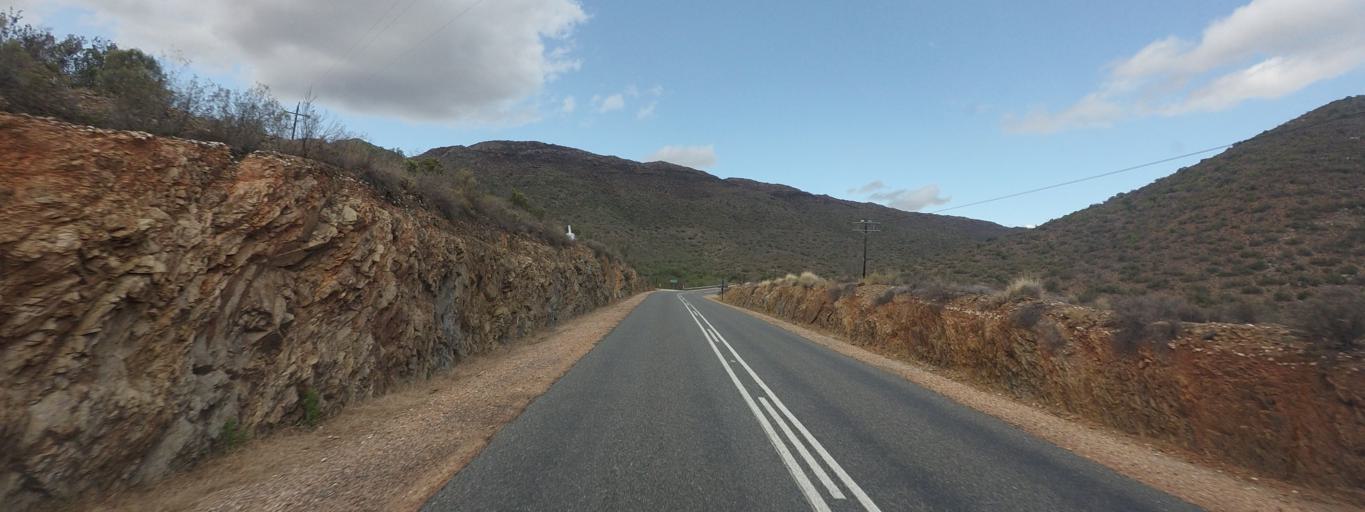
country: ZA
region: Western Cape
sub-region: Eden District Municipality
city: Ladismith
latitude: -33.4716
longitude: 21.5180
